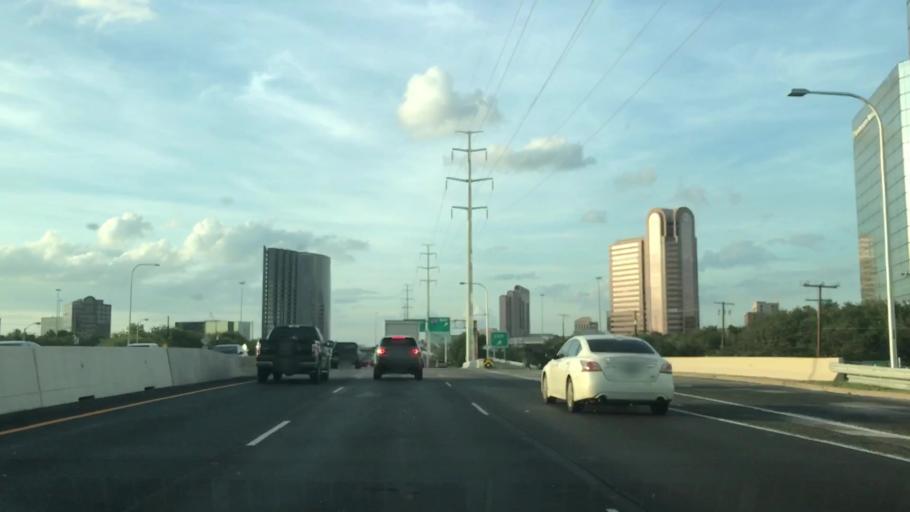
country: US
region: Texas
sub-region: Dallas County
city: Addison
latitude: 32.9212
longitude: -96.8186
